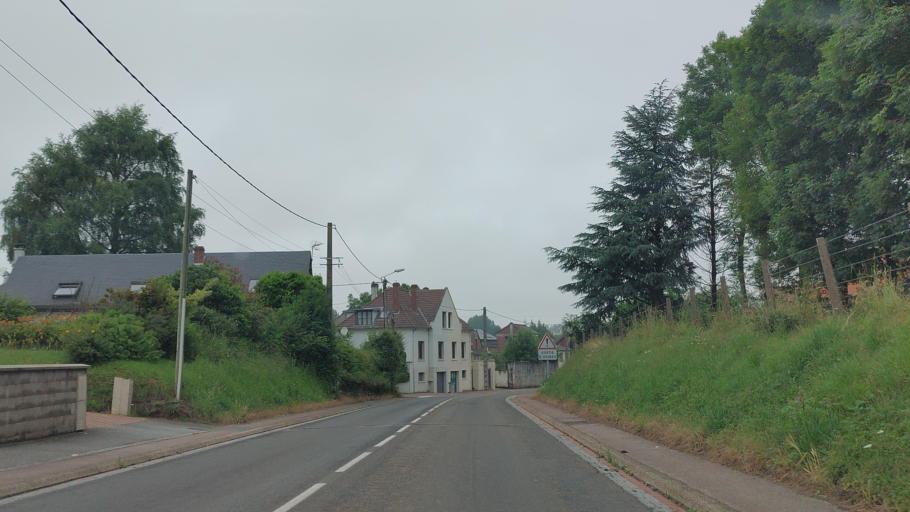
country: FR
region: Picardie
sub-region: Departement de la Somme
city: Bethencourt-sur-Mer
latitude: 50.0754
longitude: 1.5023
